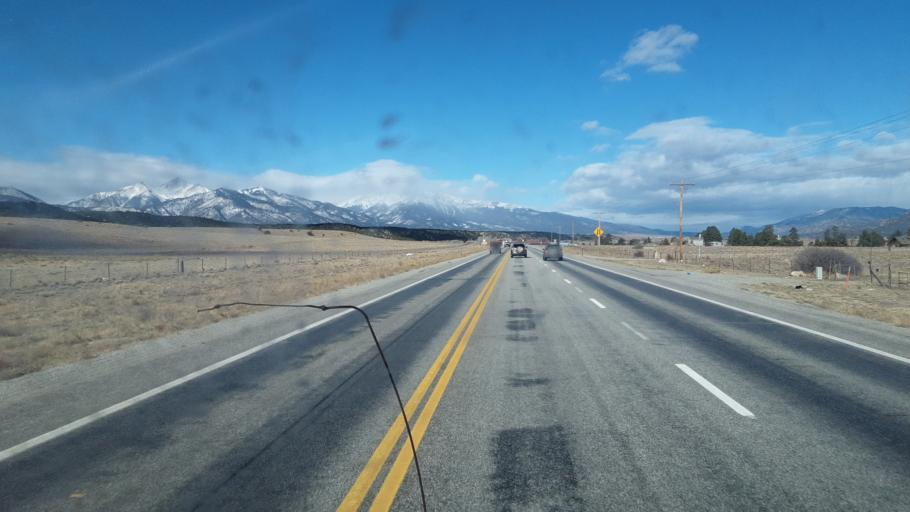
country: US
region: Colorado
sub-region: Chaffee County
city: Buena Vista
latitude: 38.7580
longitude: -106.0864
